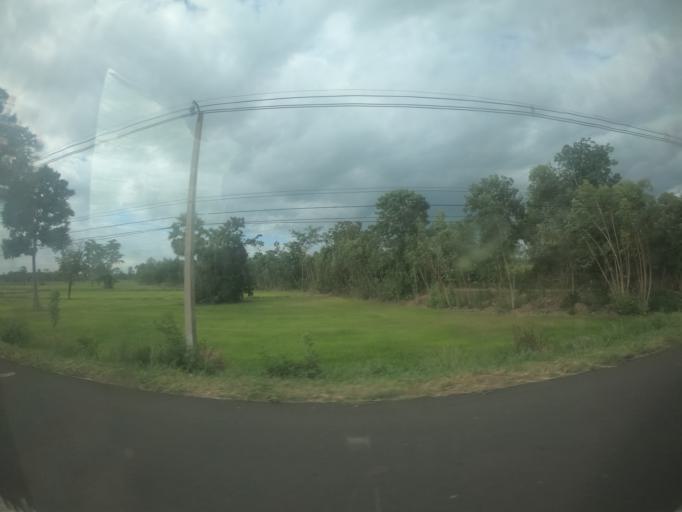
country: TH
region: Surin
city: Kap Choeng
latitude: 14.5332
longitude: 103.5283
